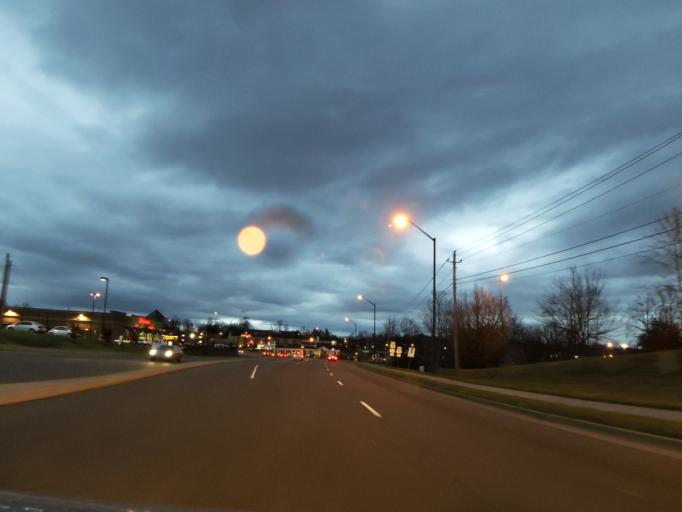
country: US
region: Tennessee
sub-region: Washington County
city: Johnson City
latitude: 36.3096
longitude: -82.3867
